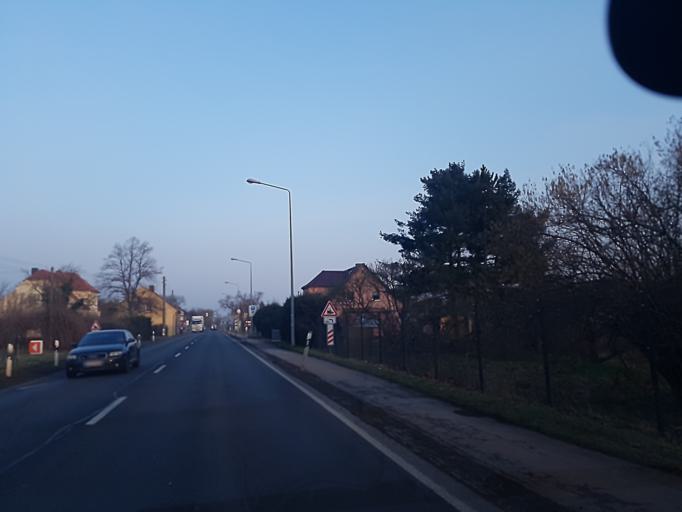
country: DE
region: Saxony-Anhalt
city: Nudersdorf
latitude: 51.8767
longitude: 12.5464
